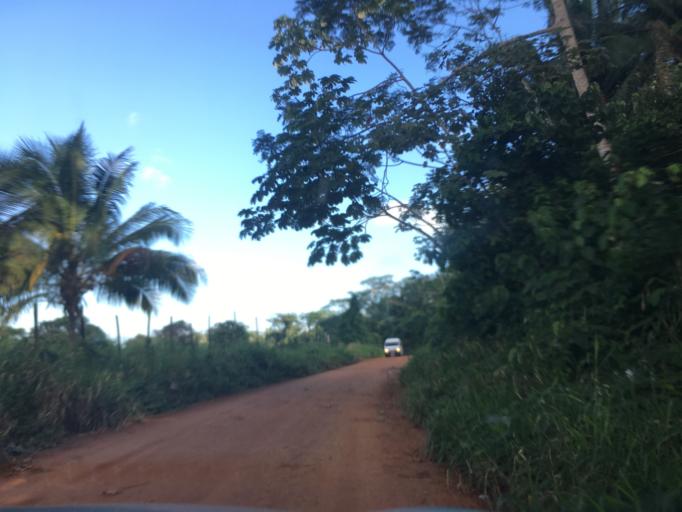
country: BZ
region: Stann Creek
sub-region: Dangriga
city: Dangriga
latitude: 16.7981
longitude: -88.3926
